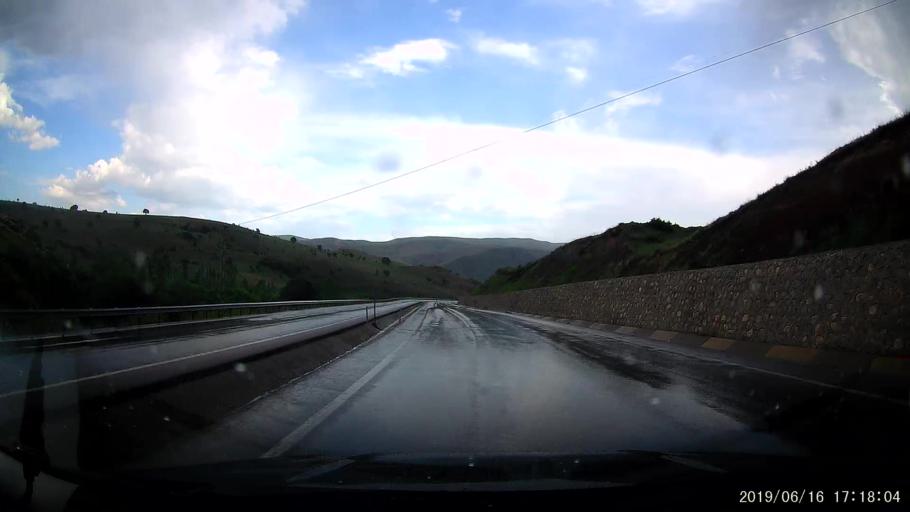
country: TR
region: Erzincan
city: Tercan
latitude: 39.8188
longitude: 40.5285
